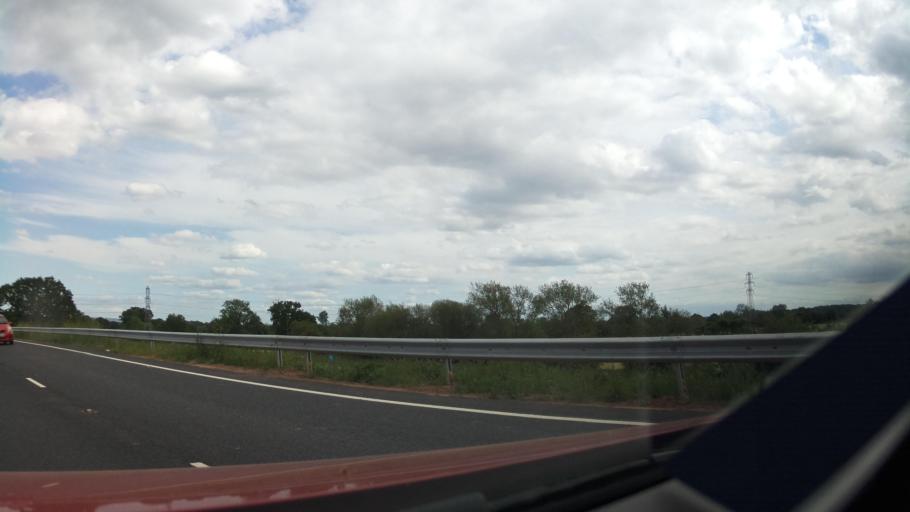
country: GB
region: England
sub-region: Worcestershire
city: Kempsey
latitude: 52.1631
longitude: -2.2297
